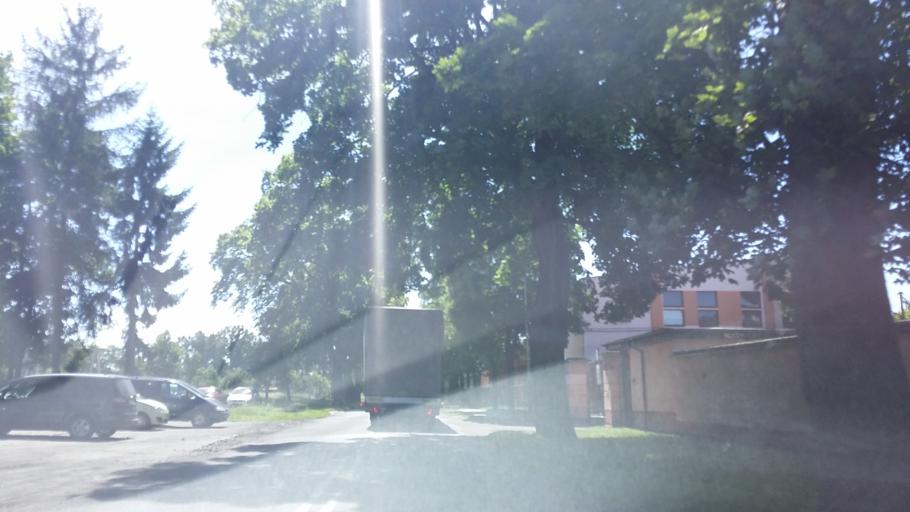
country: PL
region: West Pomeranian Voivodeship
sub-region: Powiat lobeski
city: Lobez
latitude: 53.6429
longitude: 15.6345
